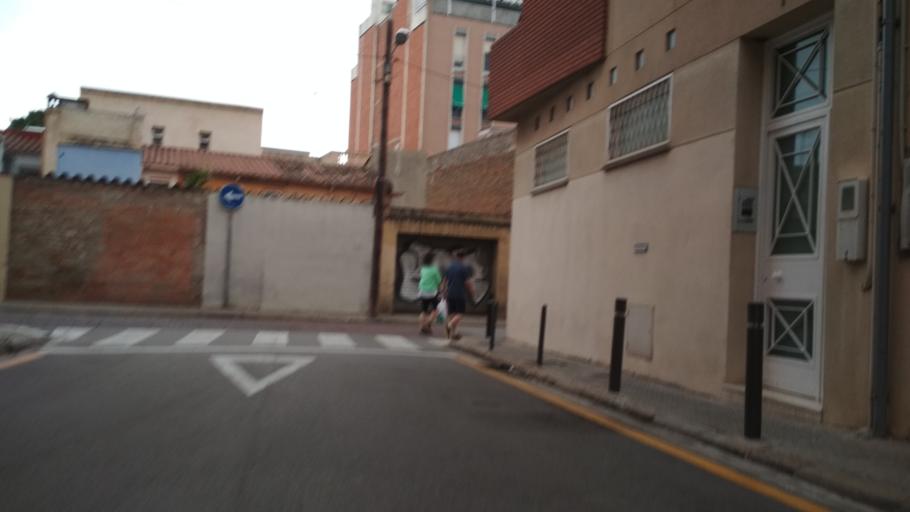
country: ES
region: Catalonia
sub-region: Provincia de Barcelona
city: Sant Andreu de Palomar
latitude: 41.4361
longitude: 2.1864
